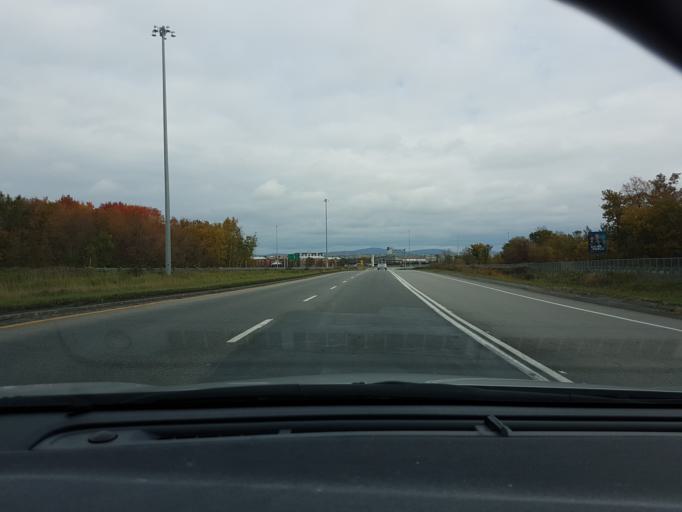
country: CA
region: Quebec
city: L'Ancienne-Lorette
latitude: 46.8223
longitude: -71.2953
